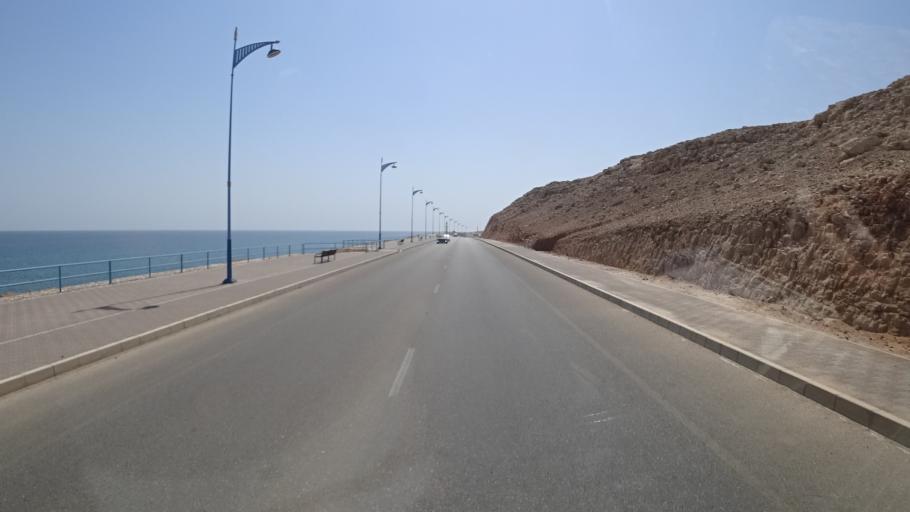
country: OM
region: Ash Sharqiyah
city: Sur
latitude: 22.5662
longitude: 59.5683
